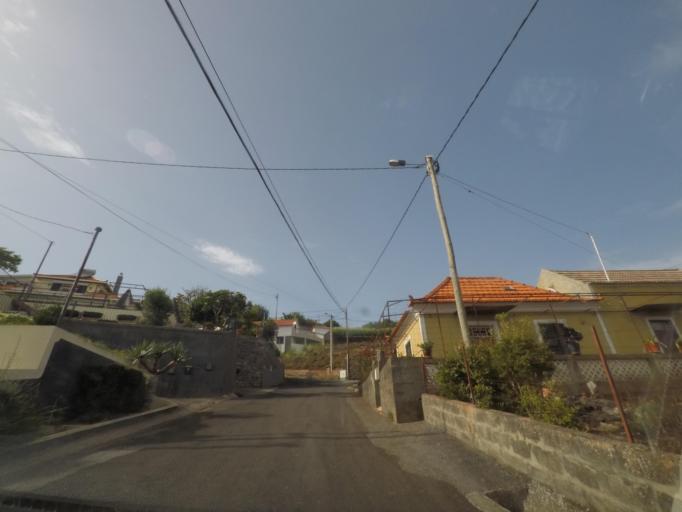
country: PT
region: Madeira
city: Ponta do Sol
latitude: 32.6953
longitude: -17.1165
